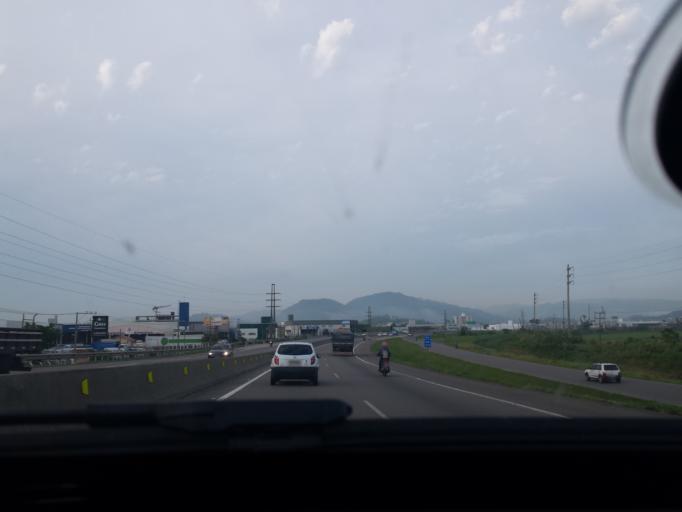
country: BR
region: Santa Catarina
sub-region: Tubarao
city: Tubarao
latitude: -28.4665
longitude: -48.9968
